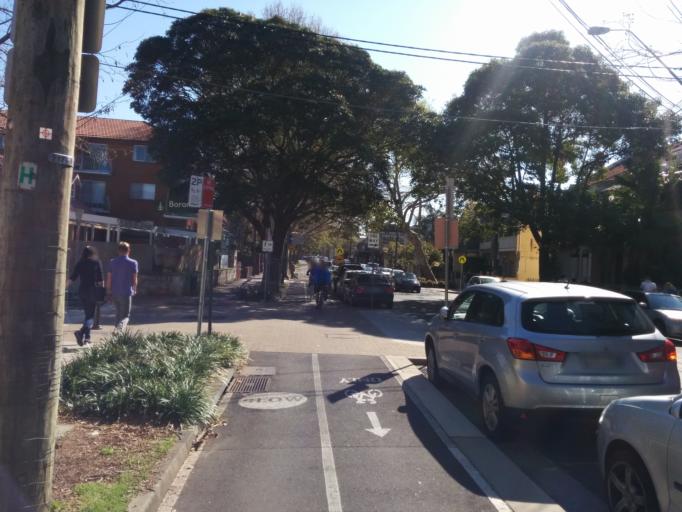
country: AU
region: New South Wales
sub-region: City of Sydney
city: Redfern
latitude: -33.8939
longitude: 151.2139
